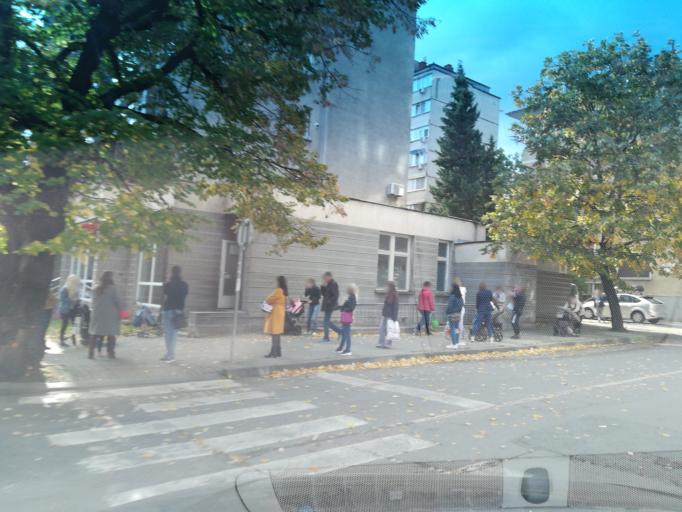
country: BG
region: Stara Zagora
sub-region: Obshtina Stara Zagora
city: Stara Zagora
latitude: 42.4305
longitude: 25.6329
